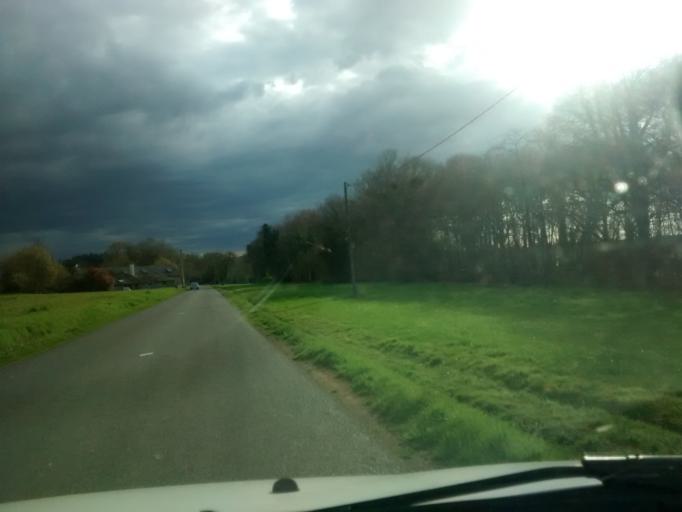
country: FR
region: Brittany
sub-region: Departement d'Ille-et-Vilaine
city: Servon-sur-Vilaine
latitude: 48.1605
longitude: -1.4880
